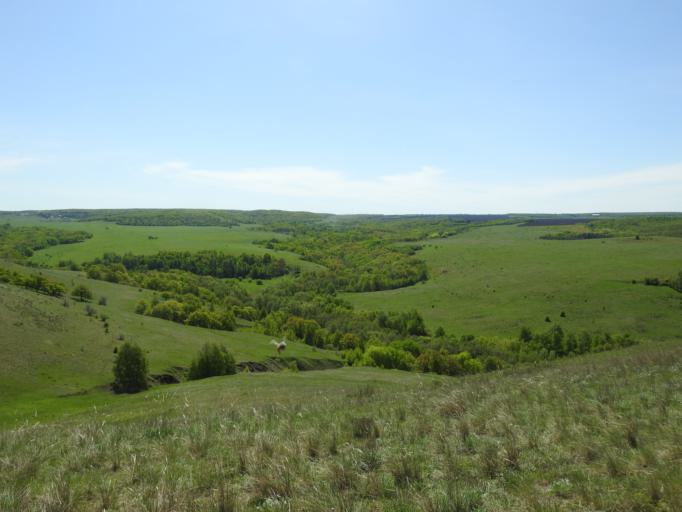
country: RU
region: Saratov
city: Krasnyy Oktyabr'
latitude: 51.5977
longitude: 45.7180
